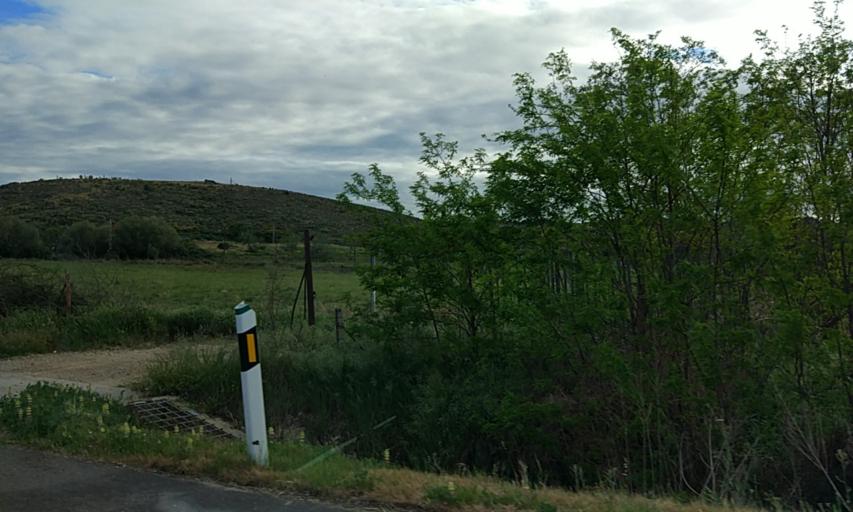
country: ES
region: Extremadura
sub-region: Provincia de Caceres
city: Coria
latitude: 39.9609
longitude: -6.5148
